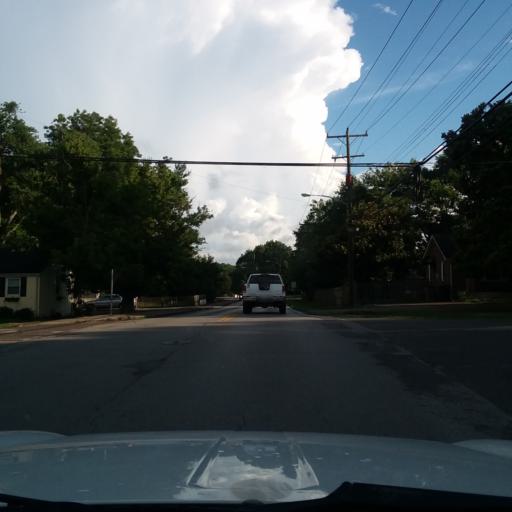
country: US
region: Tennessee
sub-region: Davidson County
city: Oak Hill
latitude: 36.0630
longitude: -86.7593
